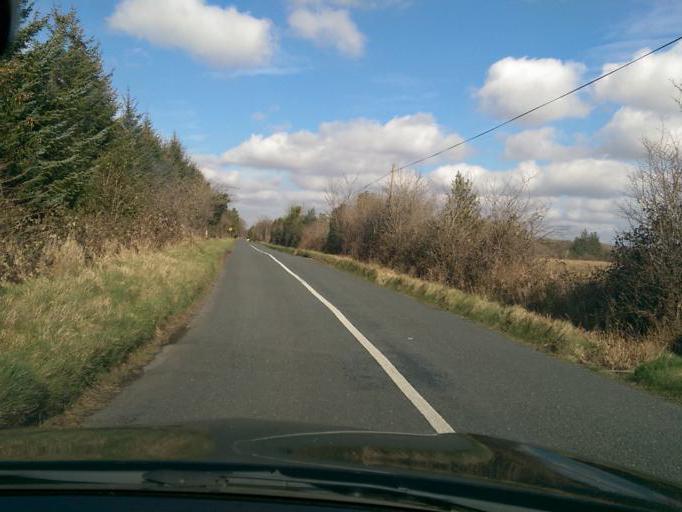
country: IE
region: Connaught
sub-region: County Galway
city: Athenry
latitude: 53.4532
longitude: -8.5503
